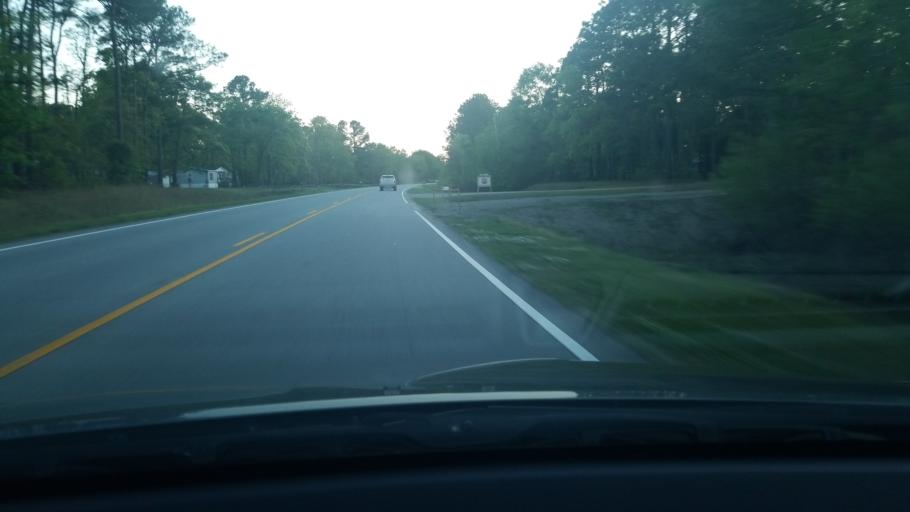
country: US
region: North Carolina
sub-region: Craven County
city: Vanceboro
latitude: 35.2362
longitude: -77.1036
